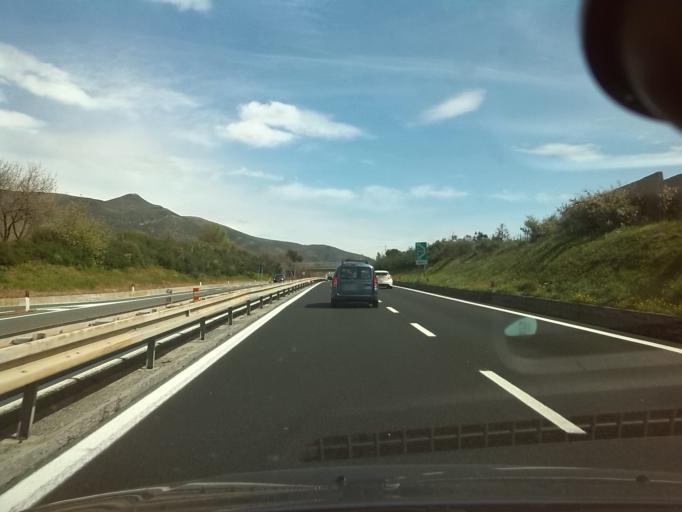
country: IT
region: Liguria
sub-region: Provincia di Savona
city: Campochiesa
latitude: 44.0771
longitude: 8.1900
